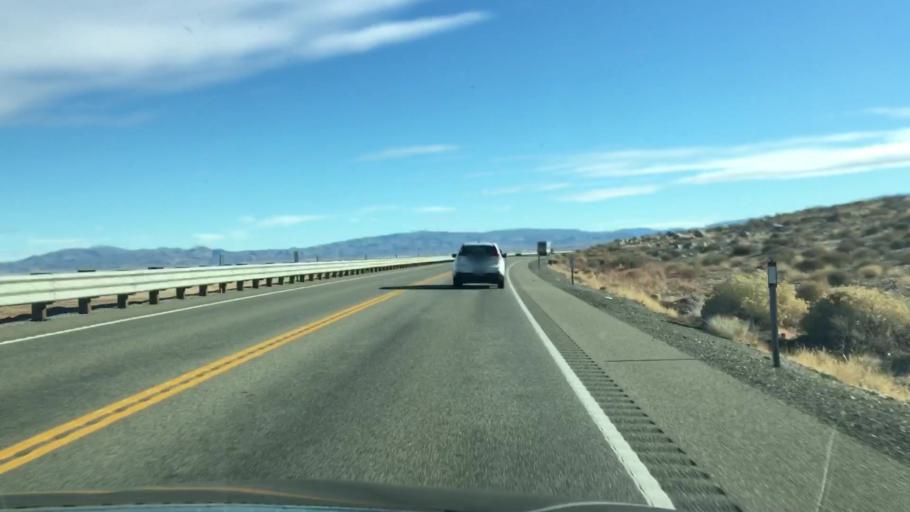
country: US
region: Nevada
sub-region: Mineral County
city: Hawthorne
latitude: 38.6093
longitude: -118.7152
